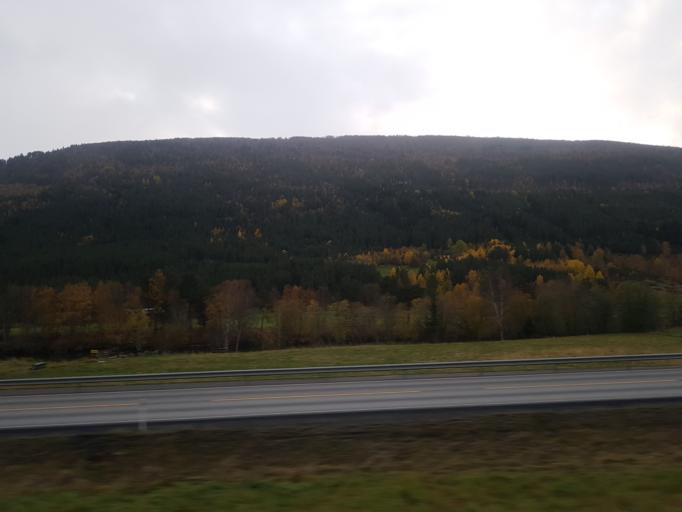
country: NO
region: Oppland
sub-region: Dovre
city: Dovre
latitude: 61.9854
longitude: 9.2419
